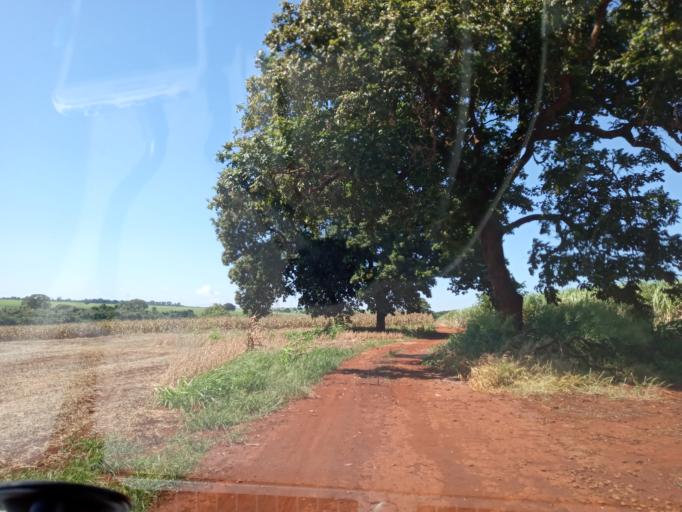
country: BR
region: Goias
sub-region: Itumbiara
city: Itumbiara
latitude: -18.4444
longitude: -49.1448
